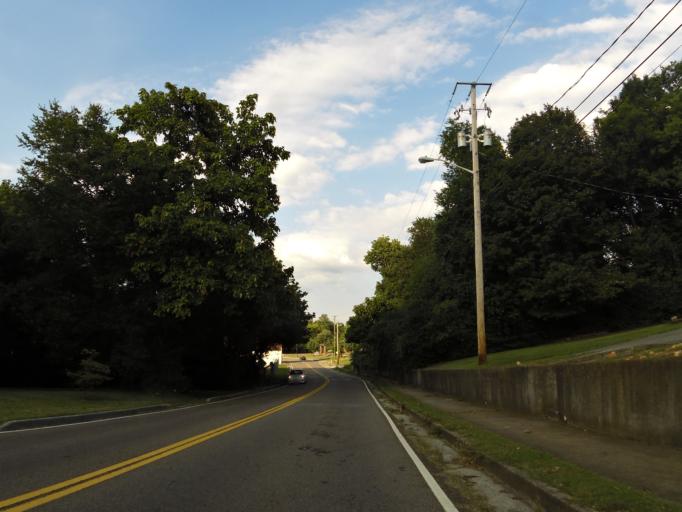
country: US
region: Tennessee
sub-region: Knox County
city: Knoxville
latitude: 35.9369
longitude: -83.9134
